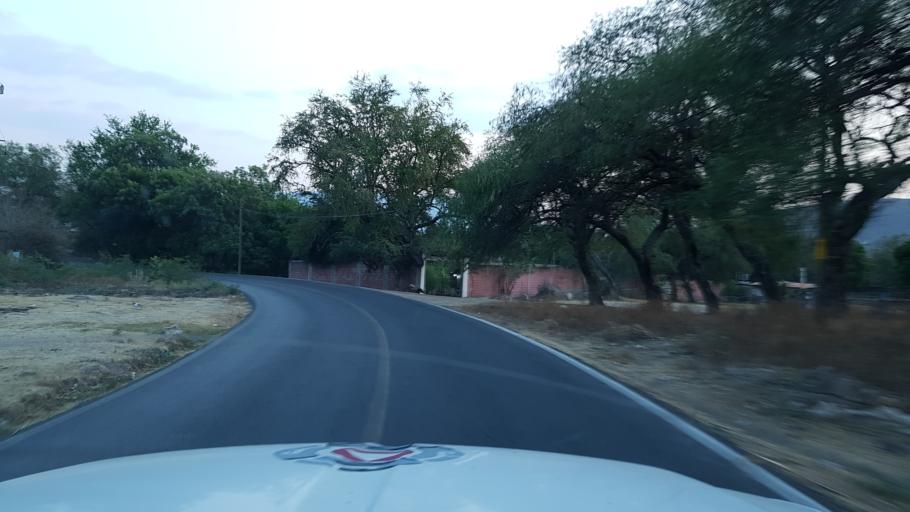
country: MX
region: Morelos
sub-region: Tlaltizapan de Zapata
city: Colonia Palo Prieto (Chipitongo)
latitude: 18.7141
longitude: -99.1094
